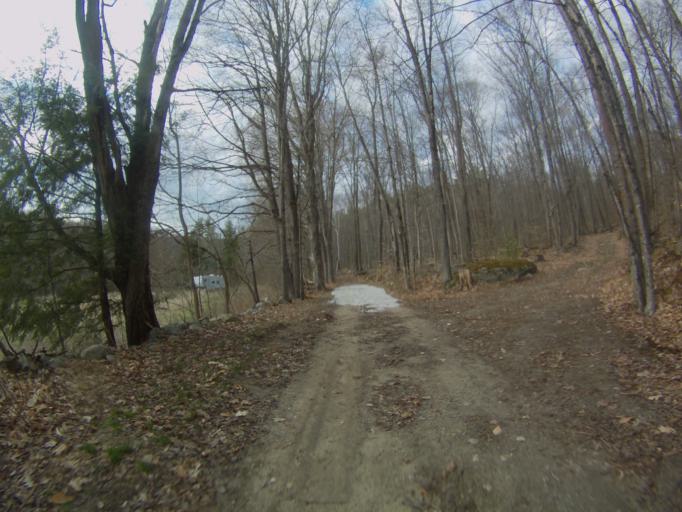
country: US
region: Vermont
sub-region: Rutland County
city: Brandon
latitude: 43.8407
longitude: -73.0413
